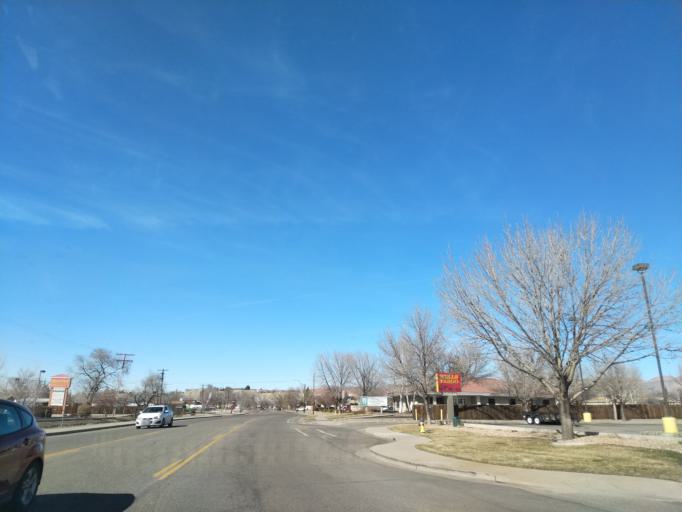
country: US
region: Colorado
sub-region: Mesa County
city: Grand Junction
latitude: 39.0782
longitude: -108.5337
